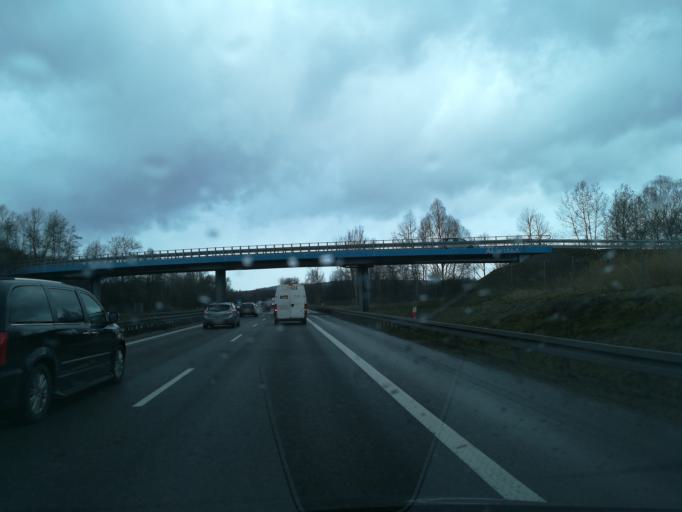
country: PL
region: Lesser Poland Voivodeship
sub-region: Krakow
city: Sidzina
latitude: 50.0058
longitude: 19.8512
